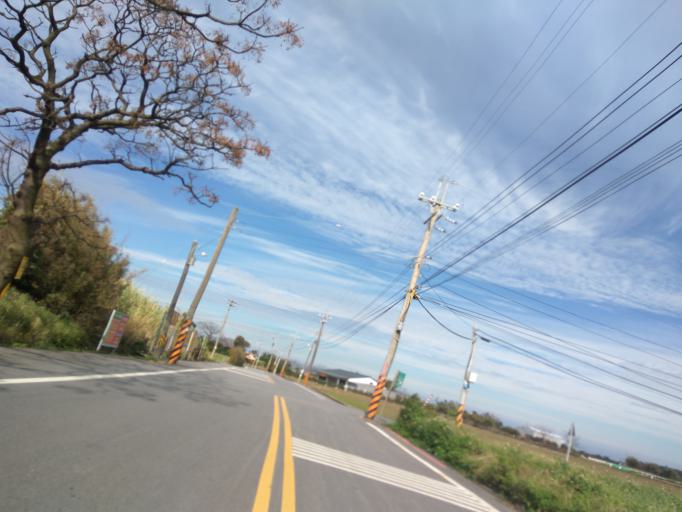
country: TW
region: Taiwan
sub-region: Hsinchu
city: Zhubei
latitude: 25.0008
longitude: 121.0873
